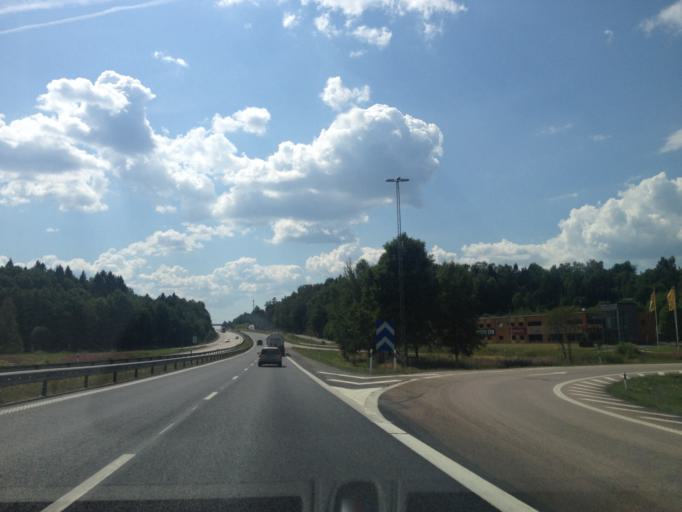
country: SE
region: Vaestra Goetaland
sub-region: Lerums Kommun
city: Stenkullen
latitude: 57.8021
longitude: 12.3669
